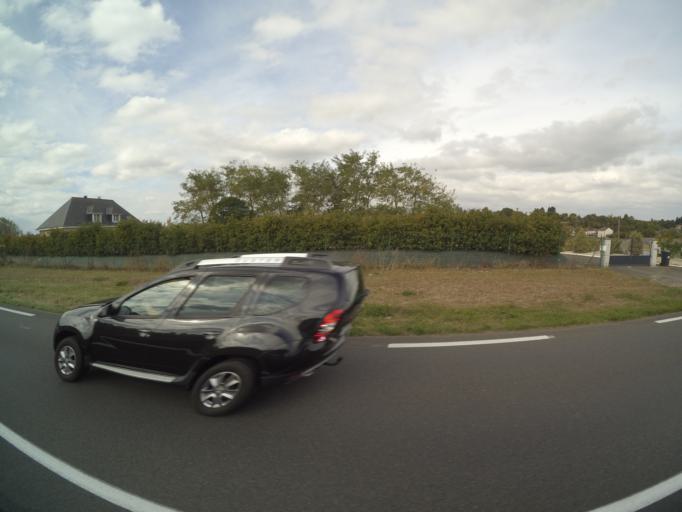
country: FR
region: Centre
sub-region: Departement d'Indre-et-Loire
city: Fondettes
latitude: 47.3859
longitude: 0.6044
